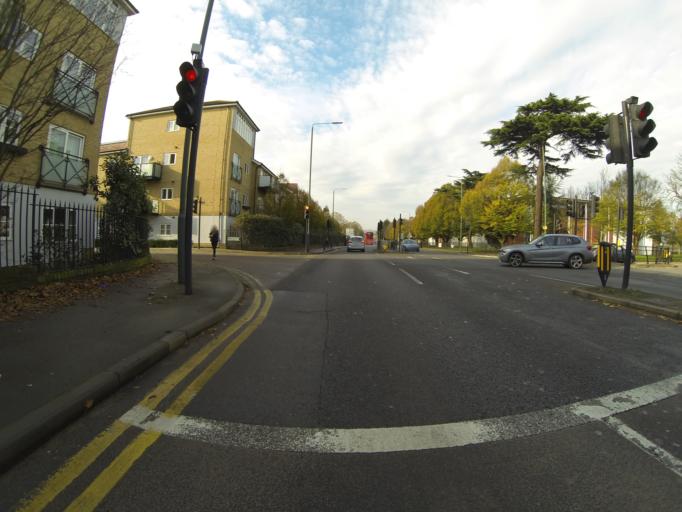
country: GB
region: England
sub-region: Greater London
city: Bexleyheath
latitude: 51.4594
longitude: 0.1261
